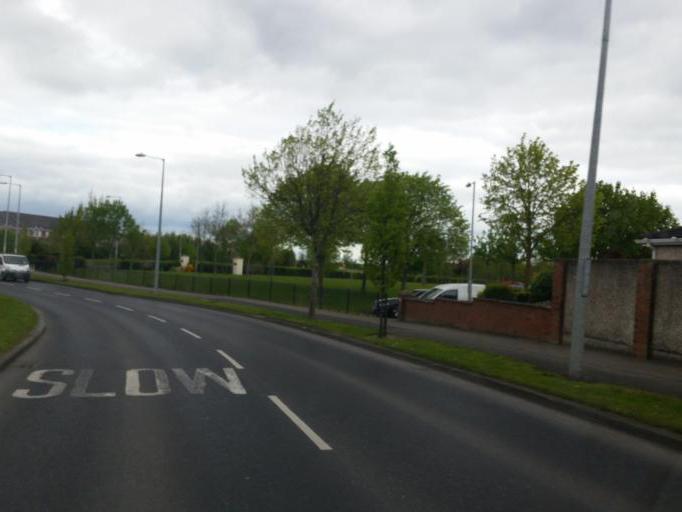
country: IE
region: Leinster
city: Hartstown
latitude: 53.3962
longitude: -6.4290
